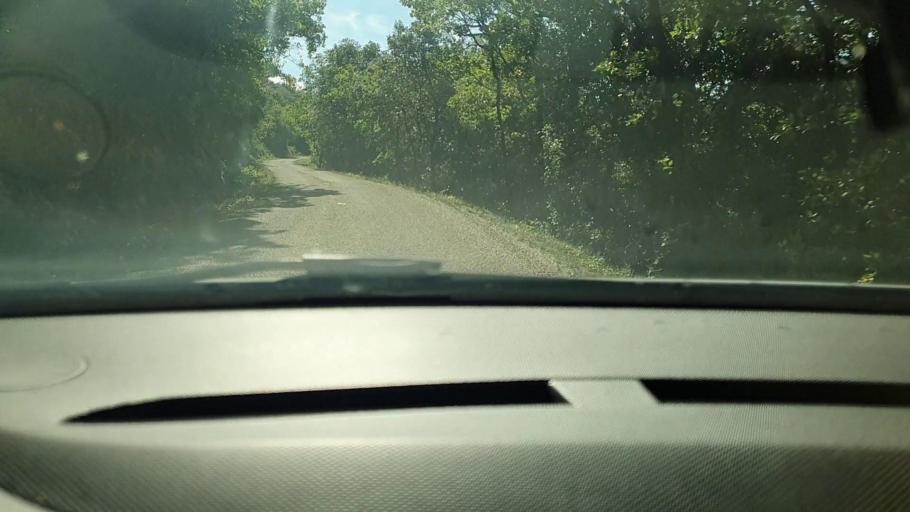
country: FR
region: Languedoc-Roussillon
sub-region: Departement du Gard
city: Barjac
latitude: 44.2035
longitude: 4.3134
